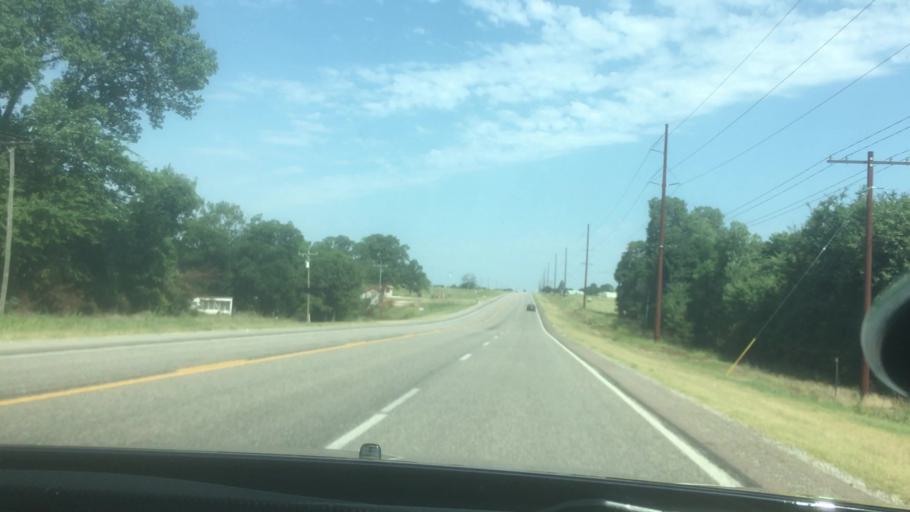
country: US
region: Oklahoma
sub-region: Seminole County
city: Konawa
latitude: 34.8461
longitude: -96.8043
